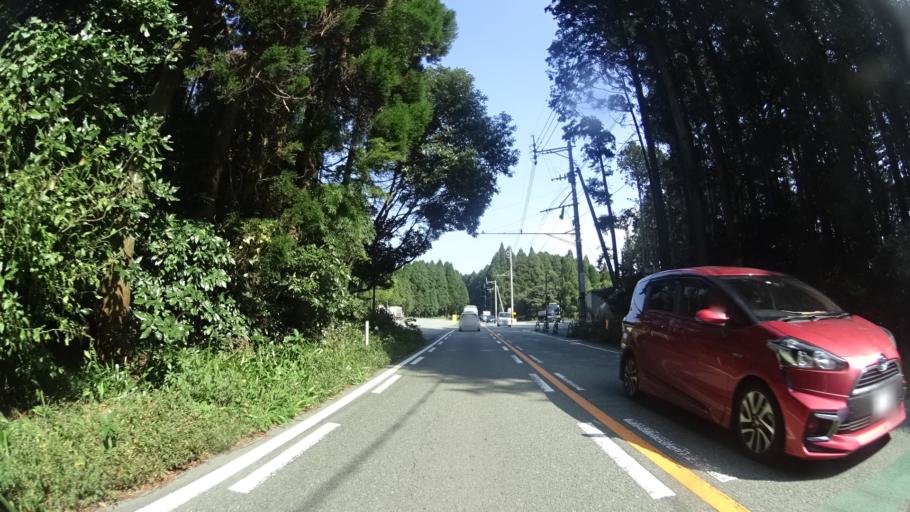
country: JP
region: Kumamoto
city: Ozu
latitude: 32.9088
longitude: 130.9493
